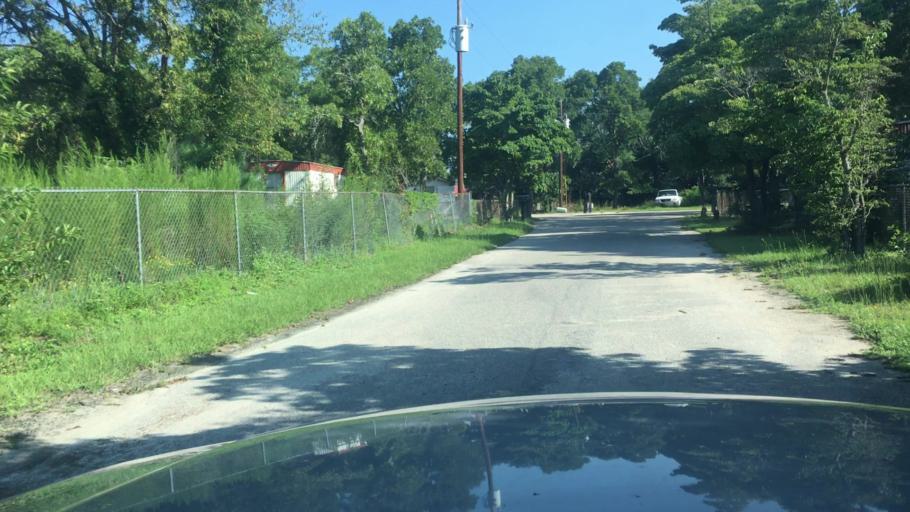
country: US
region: North Carolina
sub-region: Cumberland County
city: Spring Lake
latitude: 35.1521
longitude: -78.9165
